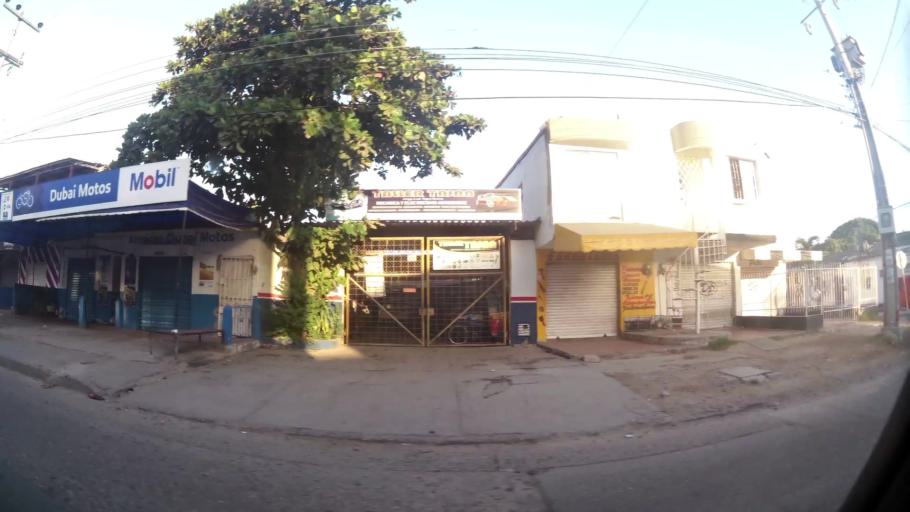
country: CO
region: Bolivar
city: Cartagena
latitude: 10.4339
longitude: -75.5296
